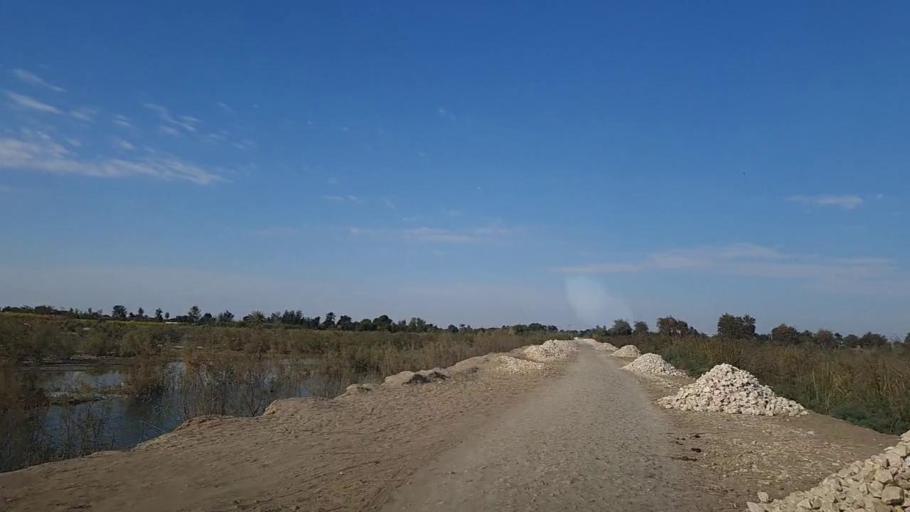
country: PK
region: Sindh
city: Khadro
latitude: 26.3025
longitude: 68.8141
